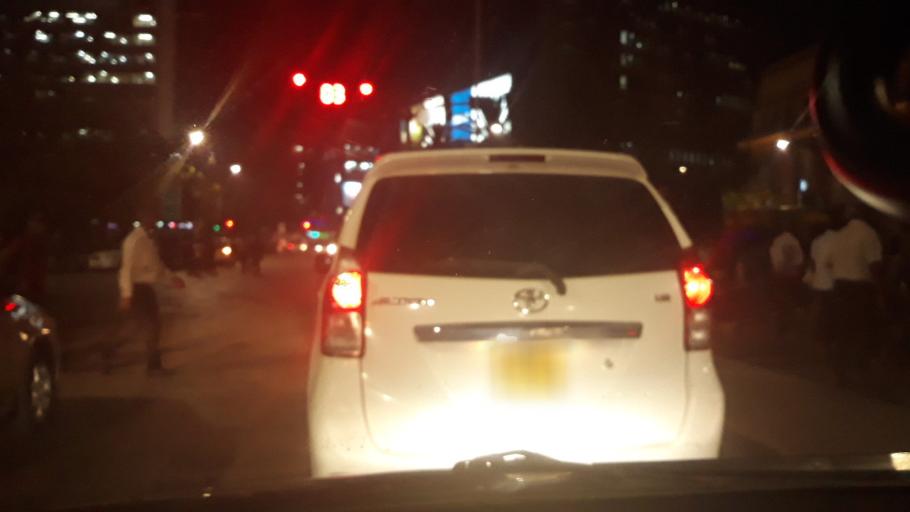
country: KE
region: Nairobi Area
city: Nairobi
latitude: -1.2855
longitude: 36.8256
